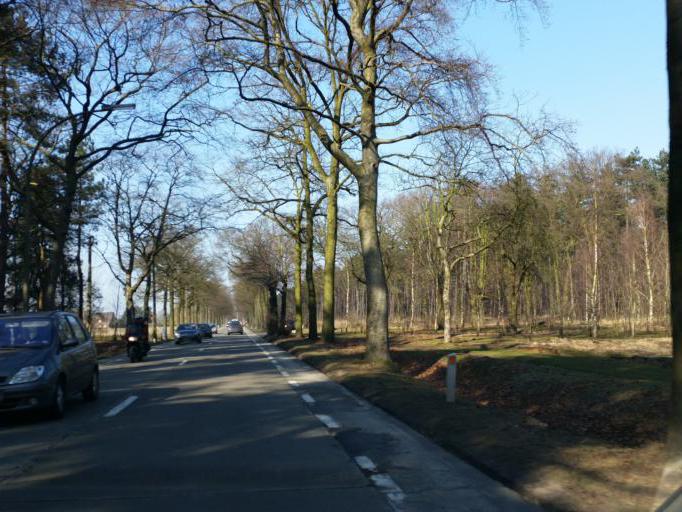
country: BE
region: Flanders
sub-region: Provincie Oost-Vlaanderen
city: Zelzate
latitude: 51.1826
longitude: 3.8375
